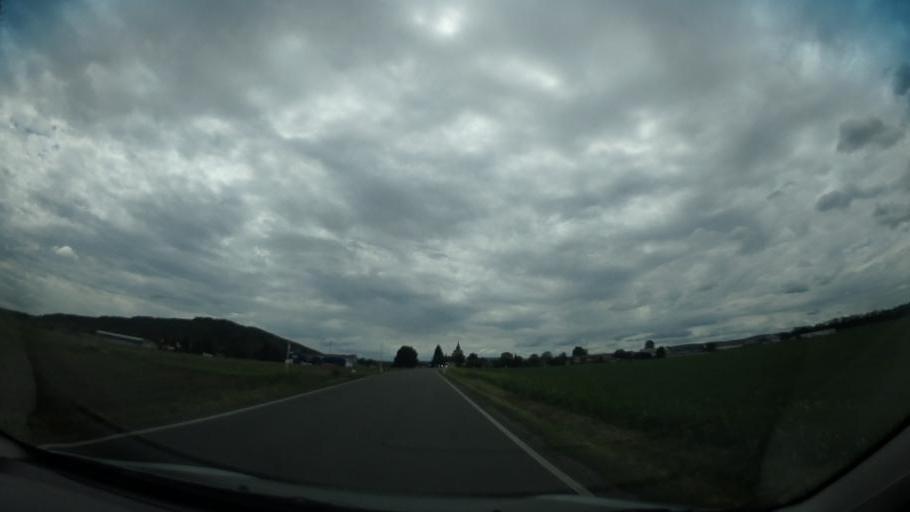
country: CZ
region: Pardubicky
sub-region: Okres Svitavy
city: Moravska Trebova
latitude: 49.7987
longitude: 16.6821
